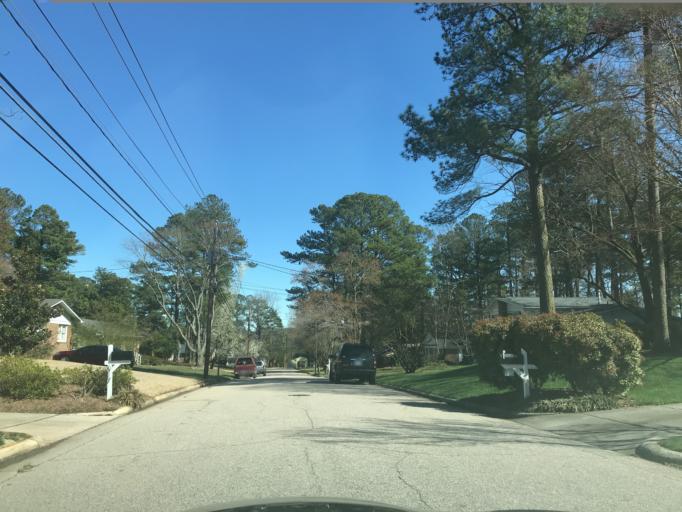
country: US
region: North Carolina
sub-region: Wake County
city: West Raleigh
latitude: 35.8506
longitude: -78.6281
